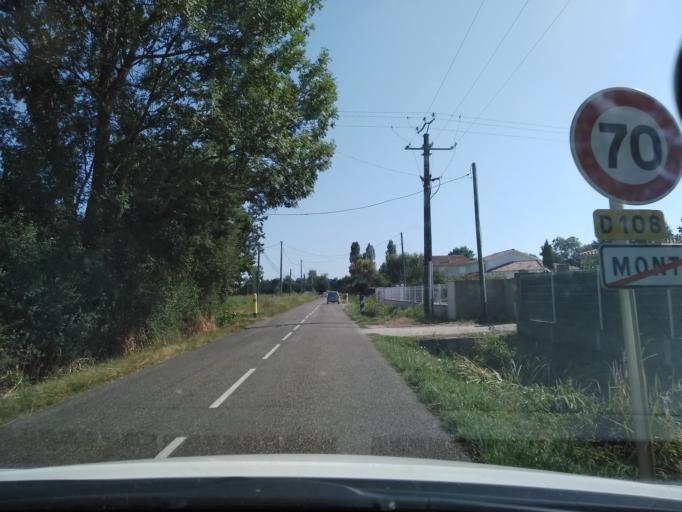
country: FR
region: Midi-Pyrenees
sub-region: Departement du Tarn-et-Garonne
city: Montech
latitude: 43.9680
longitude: 1.2401
